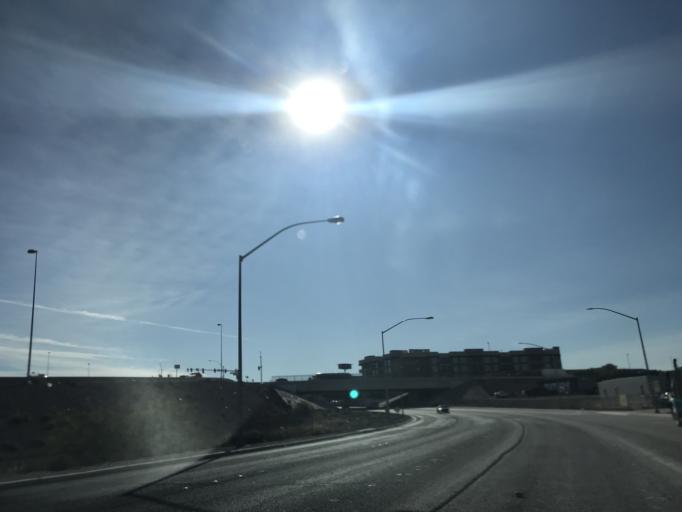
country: US
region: Nevada
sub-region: Clark County
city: Paradise
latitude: 36.0879
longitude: -115.1823
